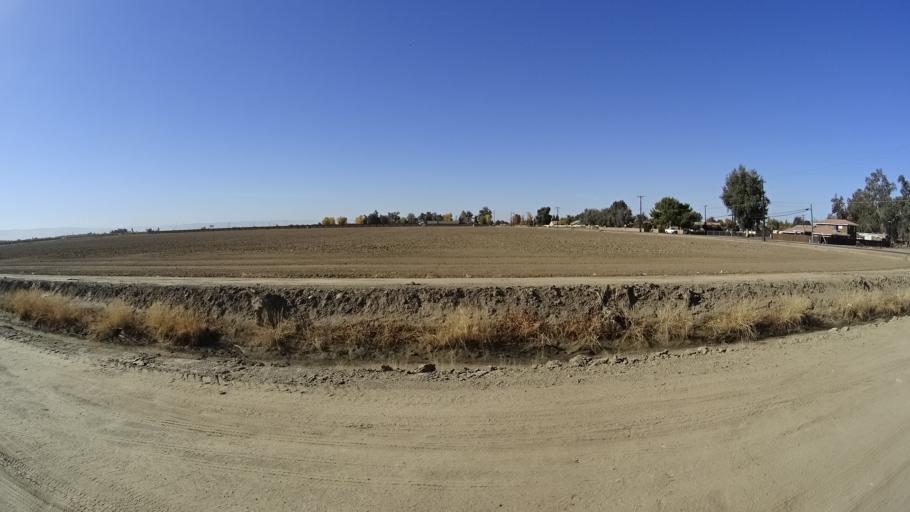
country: US
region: California
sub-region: Kern County
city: Greenfield
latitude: 35.2664
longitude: -119.0567
